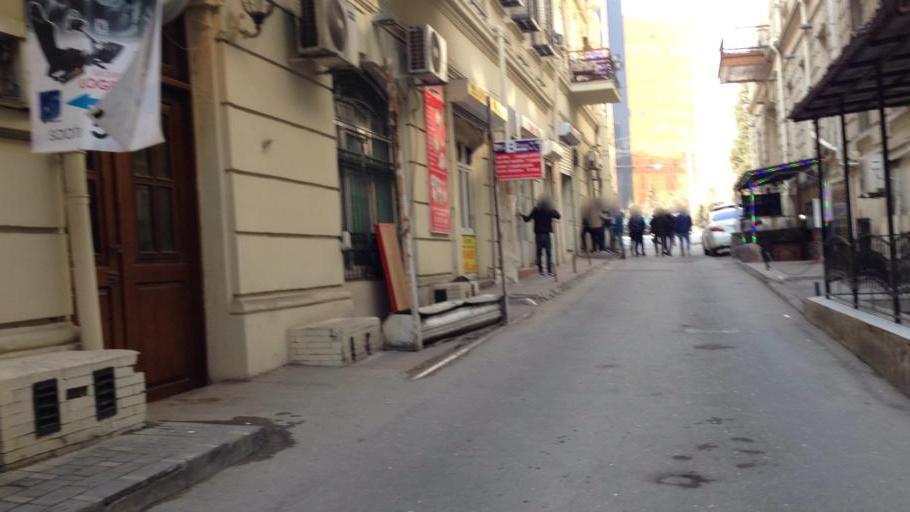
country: AZ
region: Baki
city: Baku
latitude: 40.3768
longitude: 49.8468
